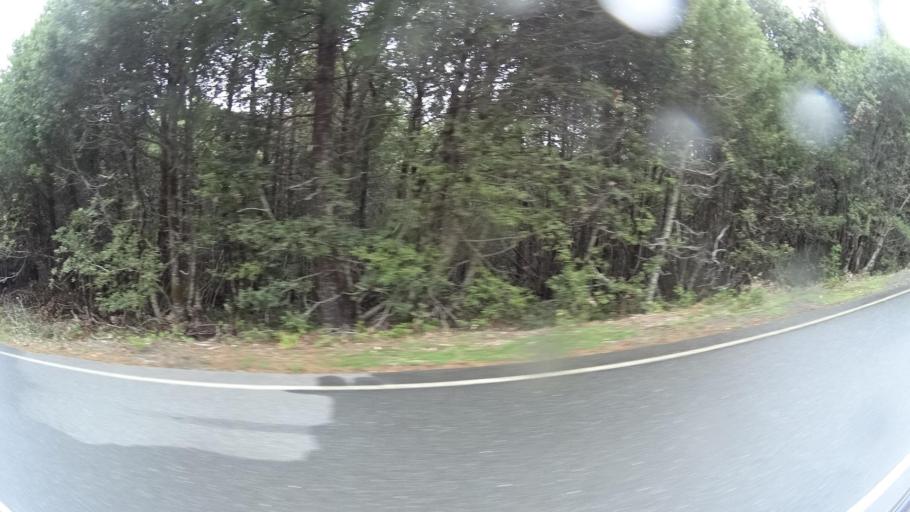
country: US
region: California
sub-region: Humboldt County
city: Willow Creek
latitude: 41.1977
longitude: -123.8066
